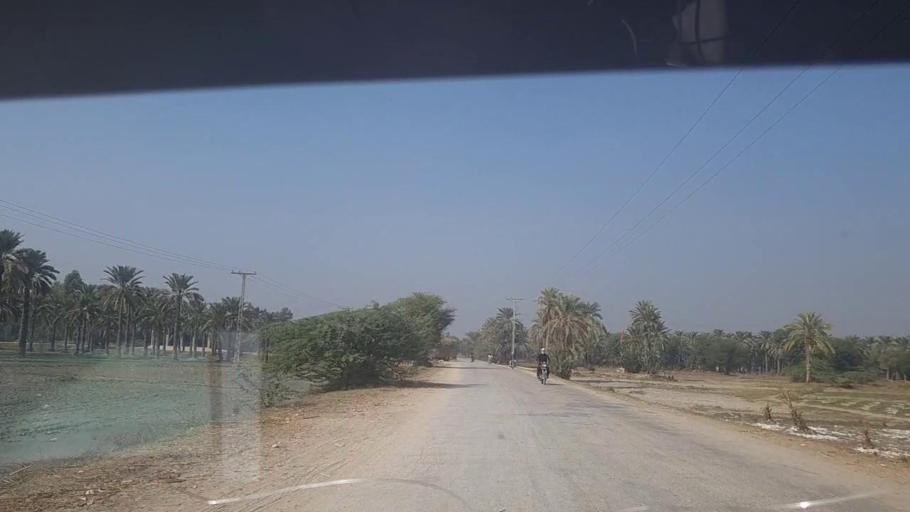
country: PK
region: Sindh
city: Kot Diji
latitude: 27.3617
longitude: 68.7072
